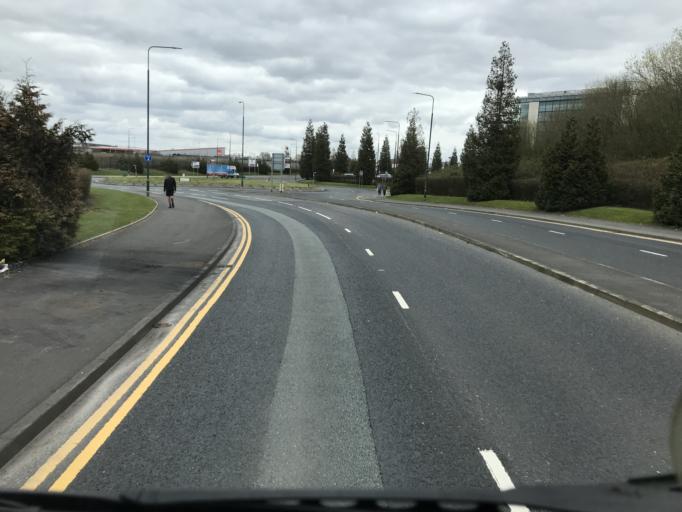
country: GB
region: England
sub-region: Trafford
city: Urmston
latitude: 53.4689
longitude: -2.3591
